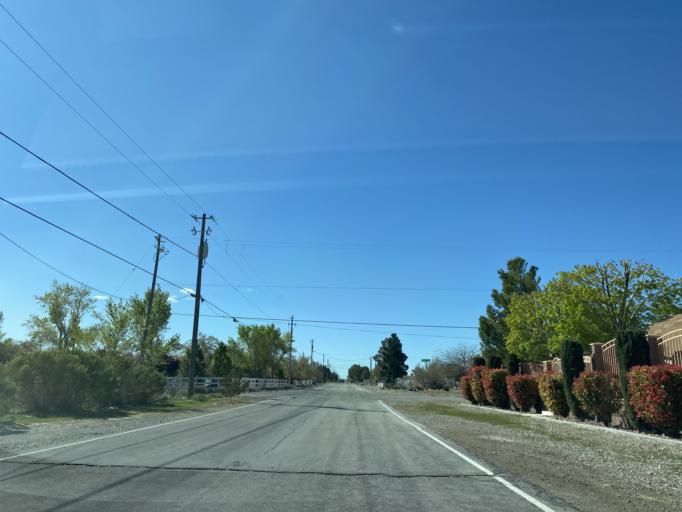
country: US
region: Nevada
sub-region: Clark County
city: North Las Vegas
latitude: 36.3325
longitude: -115.2830
